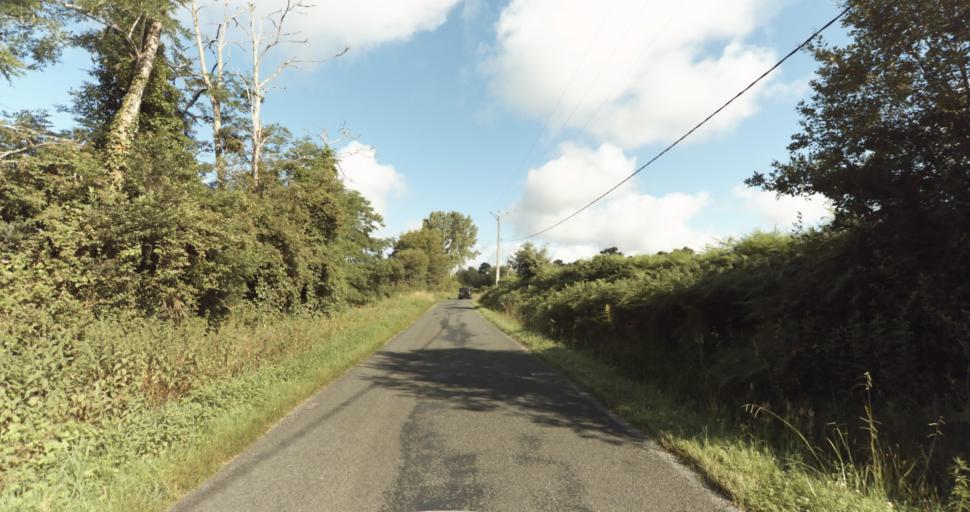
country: FR
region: Aquitaine
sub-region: Departement de la Gironde
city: Bazas
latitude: 44.4308
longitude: -0.2447
